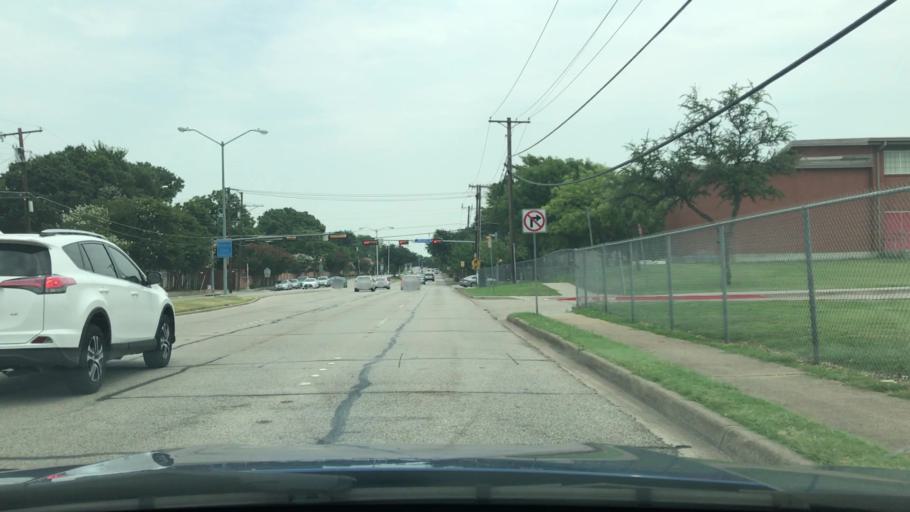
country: US
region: Texas
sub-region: Dallas County
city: Richardson
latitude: 32.9622
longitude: -96.7635
